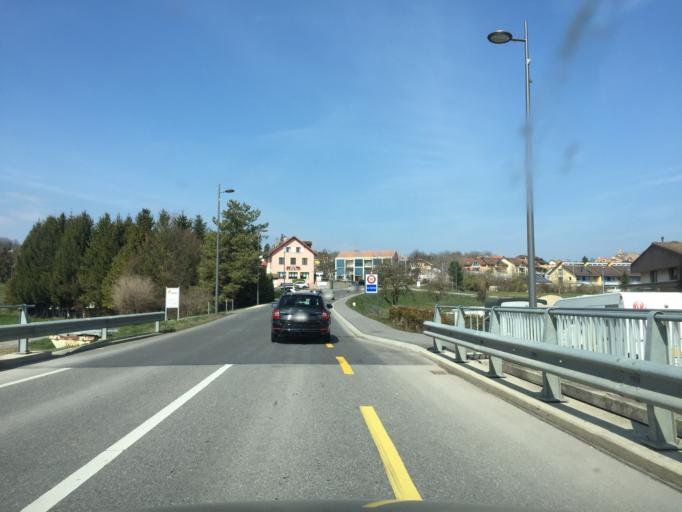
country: CH
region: Vaud
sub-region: Morges District
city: La Sarraz
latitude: 46.6536
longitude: 6.5084
